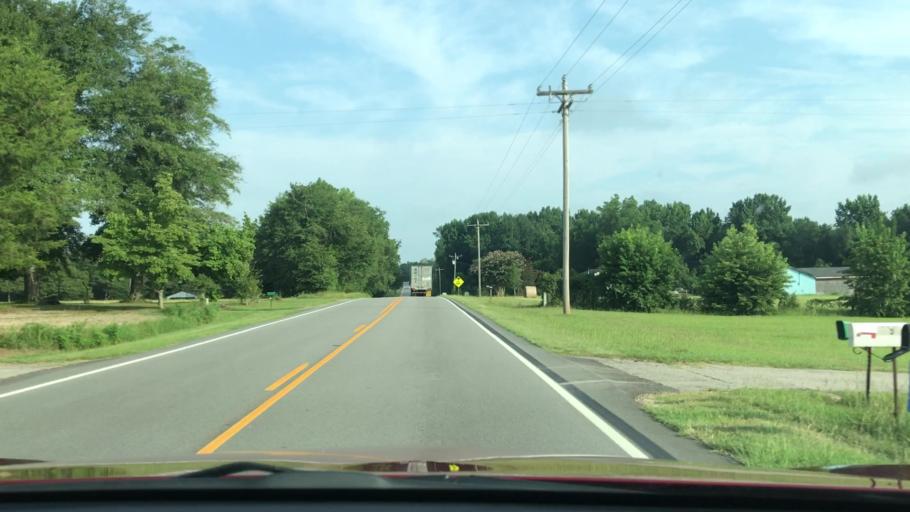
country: US
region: South Carolina
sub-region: Barnwell County
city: Blackville
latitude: 33.5555
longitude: -81.1635
